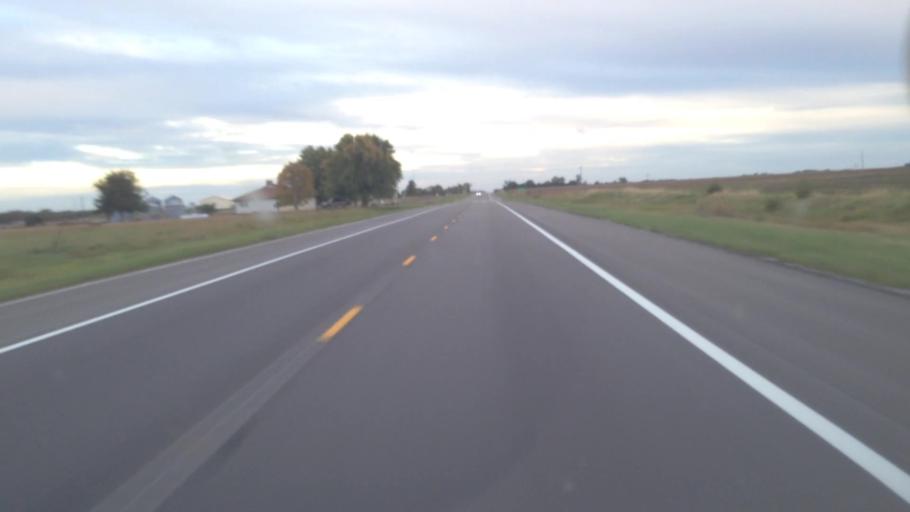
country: US
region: Kansas
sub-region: Anderson County
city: Garnett
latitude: 38.4372
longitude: -95.2487
